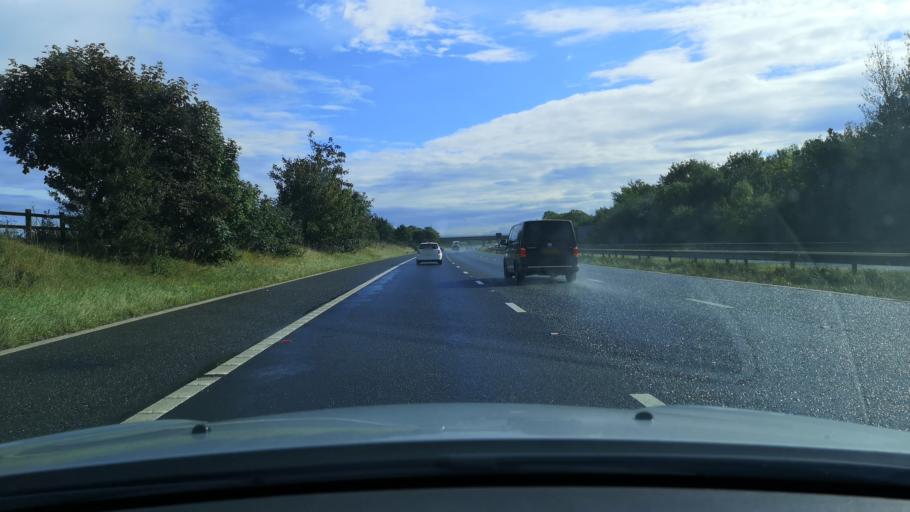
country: GB
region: England
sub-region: East Riding of Yorkshire
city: Pollington
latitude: 53.6944
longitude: -1.1257
